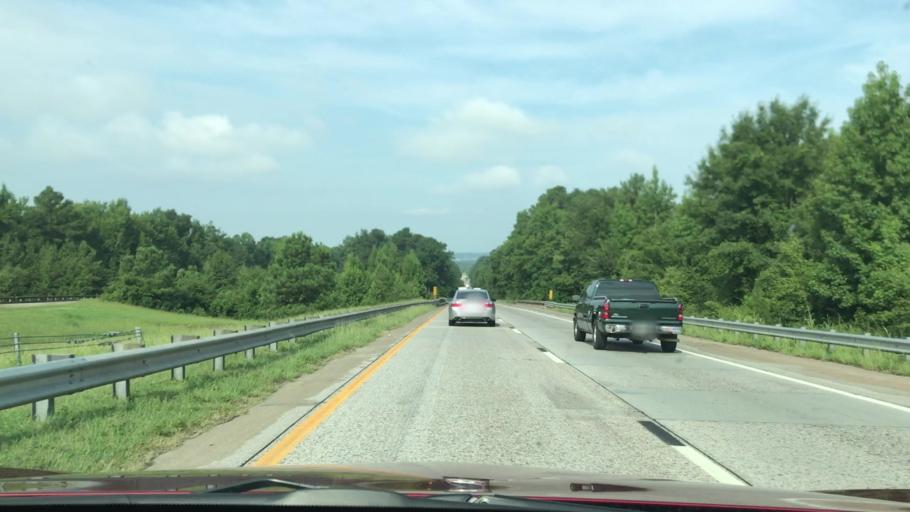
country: US
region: South Carolina
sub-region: Aiken County
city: Belvedere
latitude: 33.5463
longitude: -81.9672
